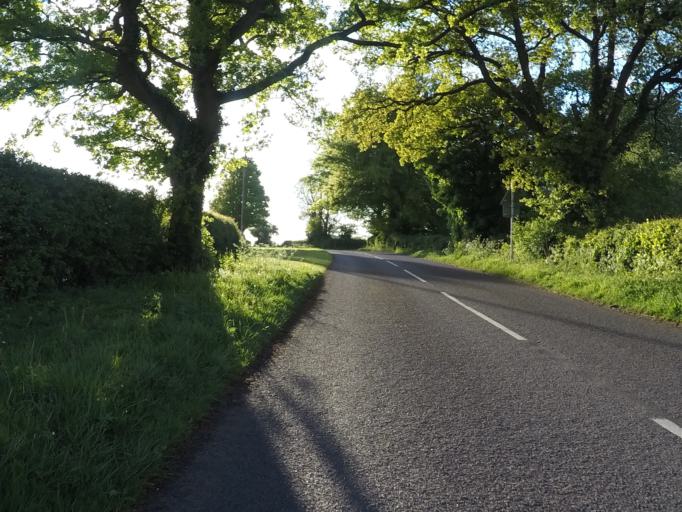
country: GB
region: England
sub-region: Oxfordshire
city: Charlbury
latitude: 51.8670
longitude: -1.4581
